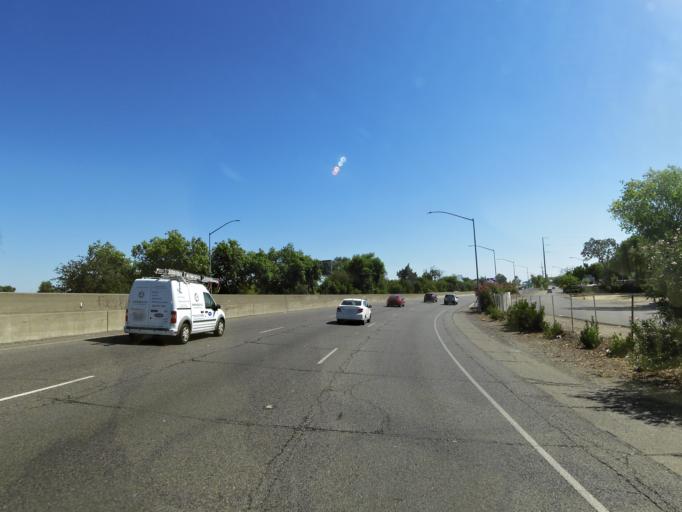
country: US
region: California
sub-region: Sacramento County
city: Arden-Arcade
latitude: 38.6238
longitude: -121.4184
